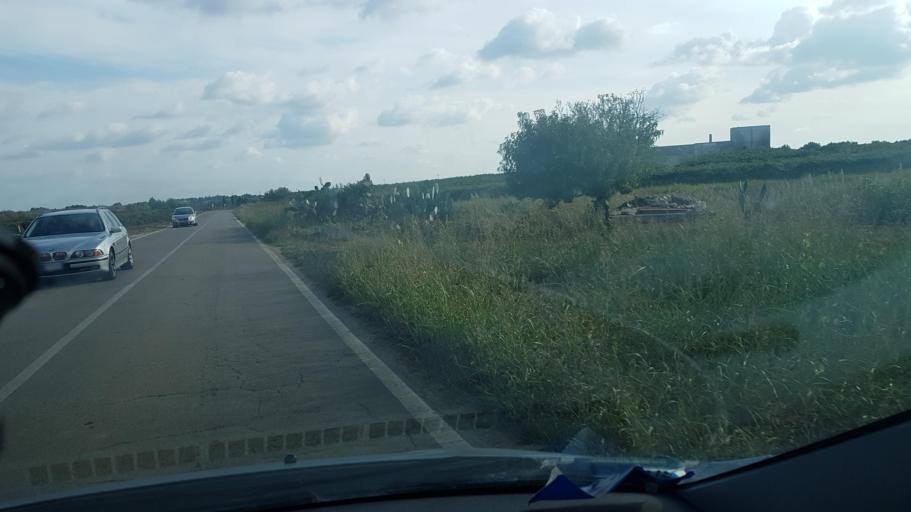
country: IT
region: Apulia
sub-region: Provincia di Lecce
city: Guagnano
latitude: 40.4269
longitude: 17.9498
